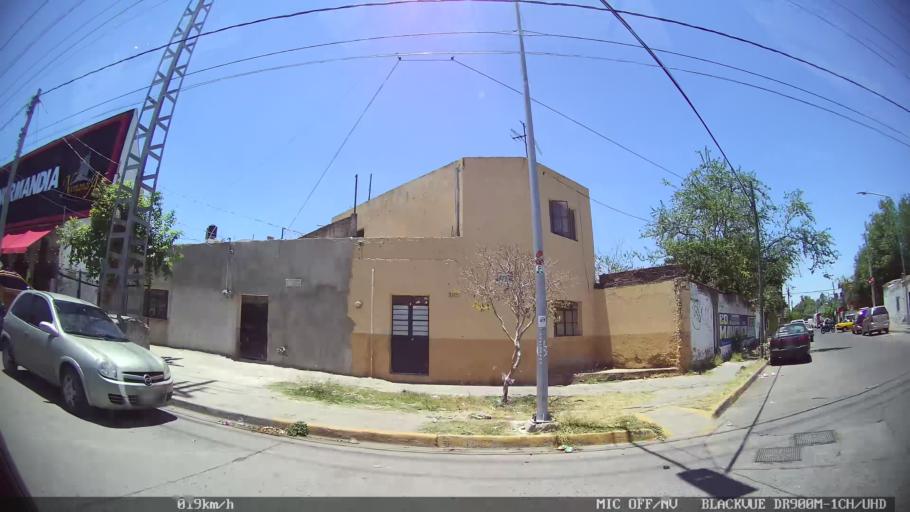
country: MX
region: Jalisco
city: Tlaquepaque
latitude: 20.6630
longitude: -103.2915
